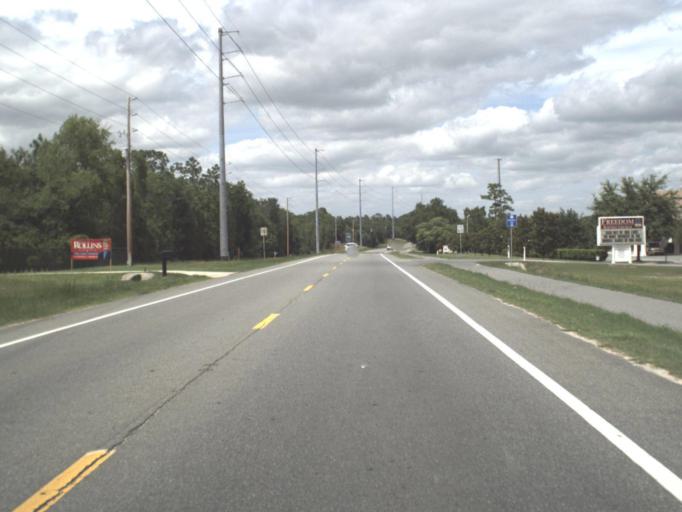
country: US
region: Florida
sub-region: Clay County
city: Keystone Heights
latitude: 29.8014
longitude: -82.0178
